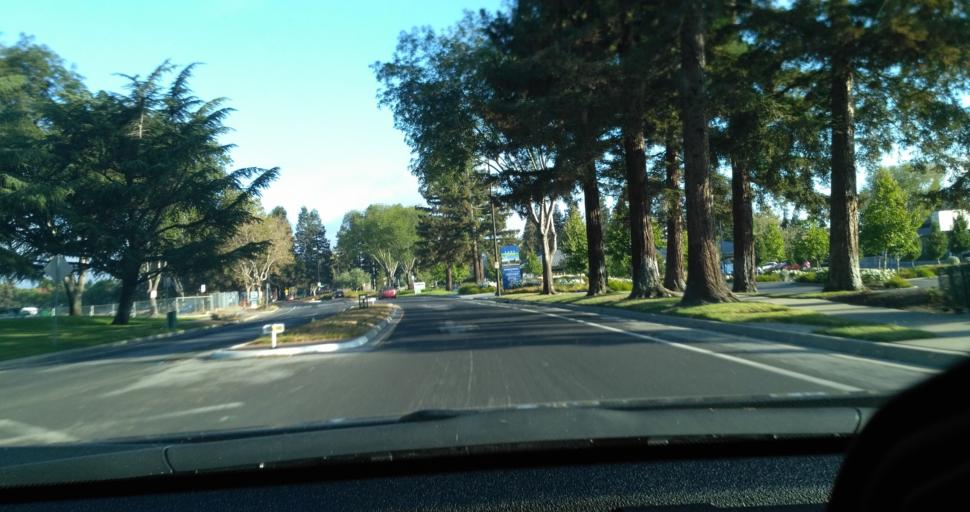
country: US
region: California
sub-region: Santa Clara County
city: Santa Clara
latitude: 37.3879
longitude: -121.9336
